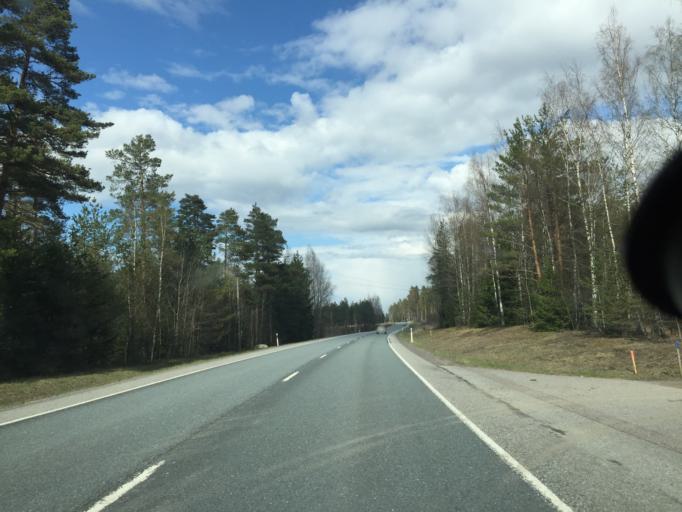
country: FI
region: Uusimaa
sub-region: Raaseporin
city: Inga
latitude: 60.1461
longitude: 23.8939
